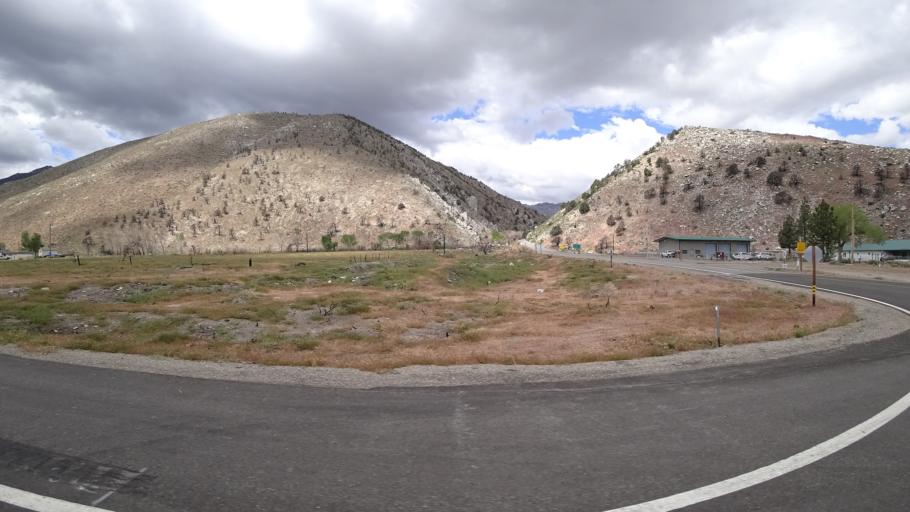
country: US
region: Nevada
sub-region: Lyon County
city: Smith Valley
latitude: 38.6426
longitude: -119.5276
